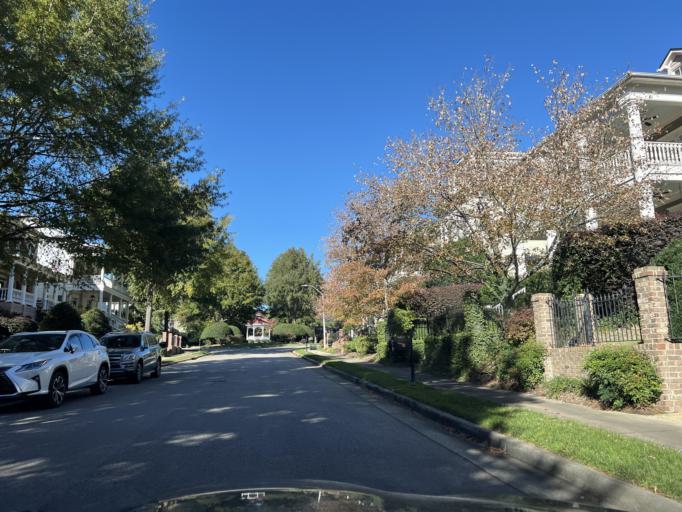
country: US
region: North Carolina
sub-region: Wake County
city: West Raleigh
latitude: 35.8939
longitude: -78.6457
